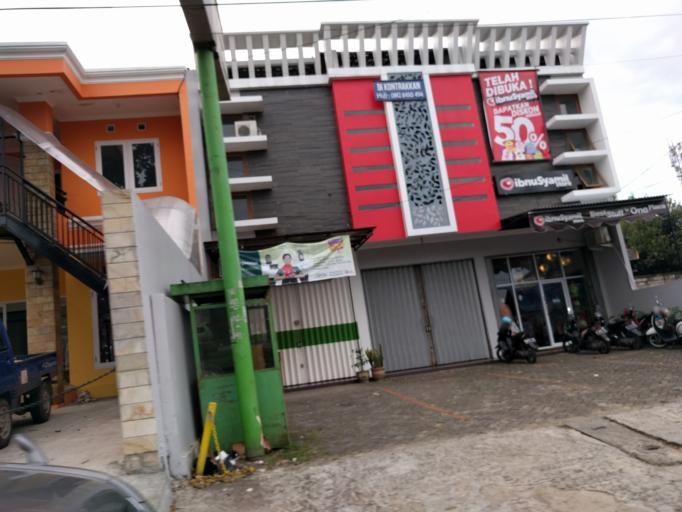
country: ID
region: West Java
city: Bogor
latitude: -6.5845
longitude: 106.8171
